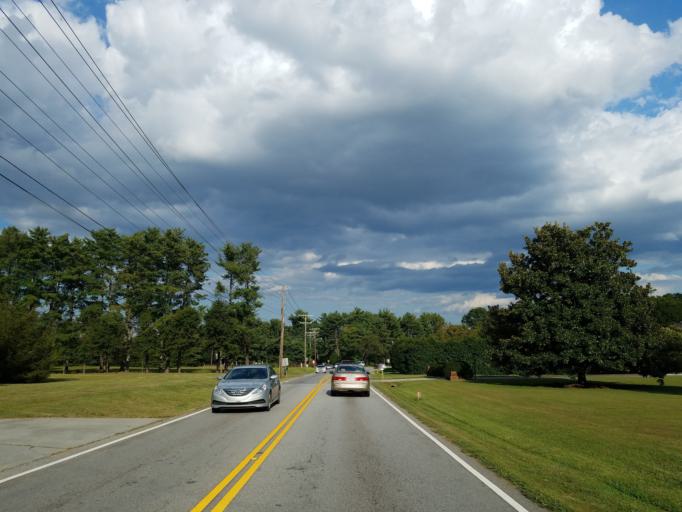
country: US
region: South Carolina
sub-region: Greenville County
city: Wade Hampton
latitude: 34.8462
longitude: -82.3037
